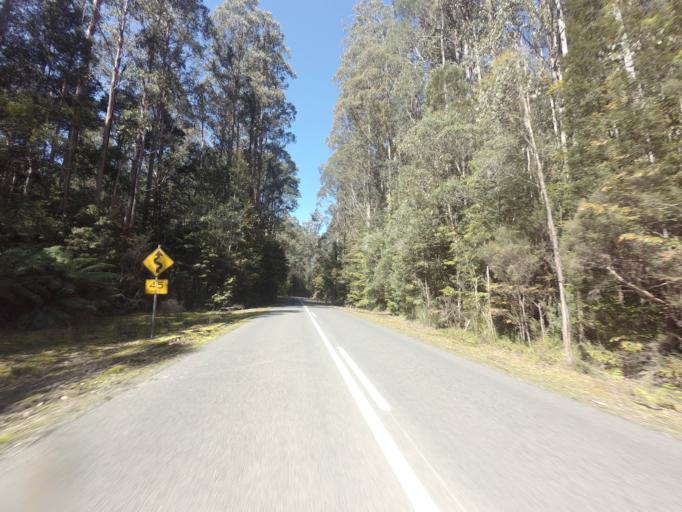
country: AU
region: Tasmania
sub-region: Huon Valley
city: Geeveston
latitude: -42.8191
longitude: 146.3066
